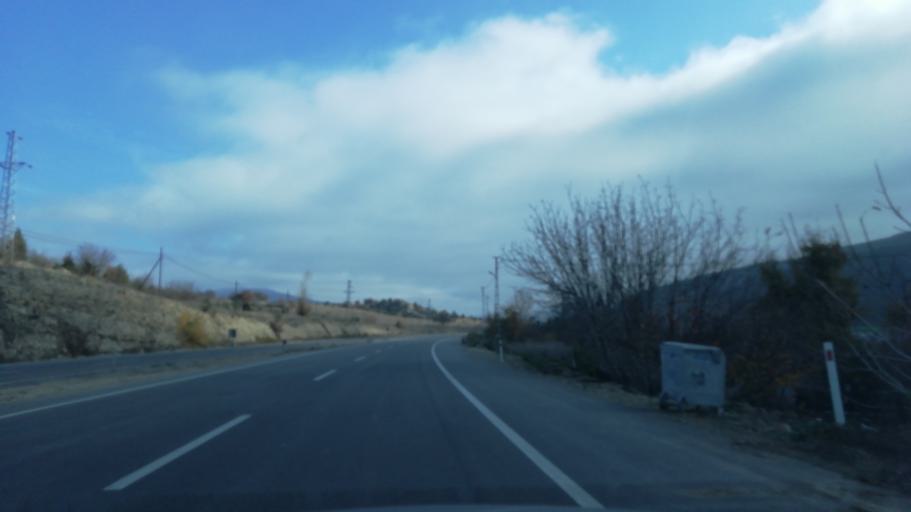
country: TR
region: Karabuk
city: Safranbolu
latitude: 41.2183
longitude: 32.7451
